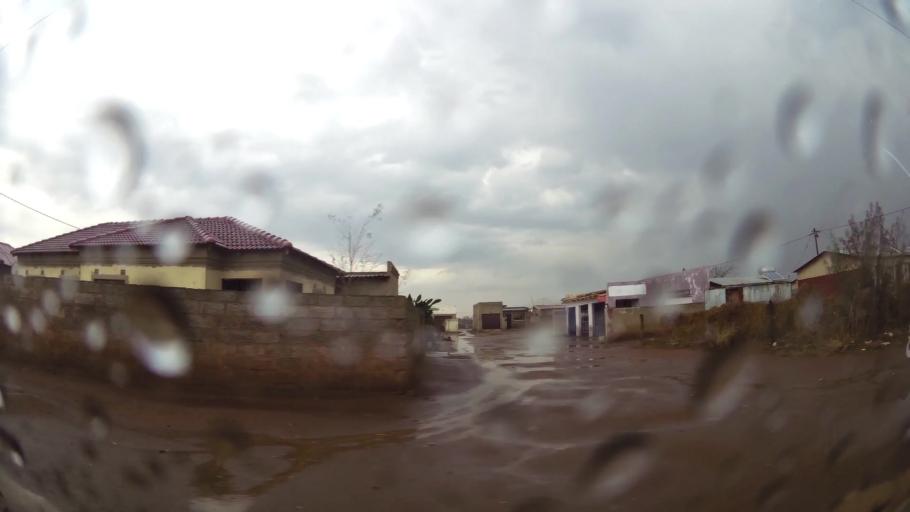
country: ZA
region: Gauteng
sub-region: Ekurhuleni Metropolitan Municipality
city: Germiston
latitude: -26.3739
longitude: 28.1510
